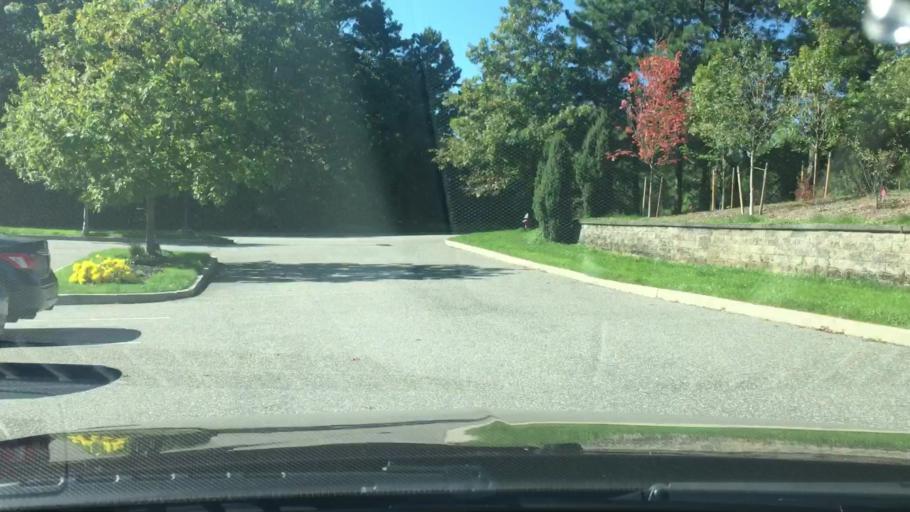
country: US
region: New York
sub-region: Suffolk County
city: Yaphank
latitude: 40.8477
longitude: -72.8762
